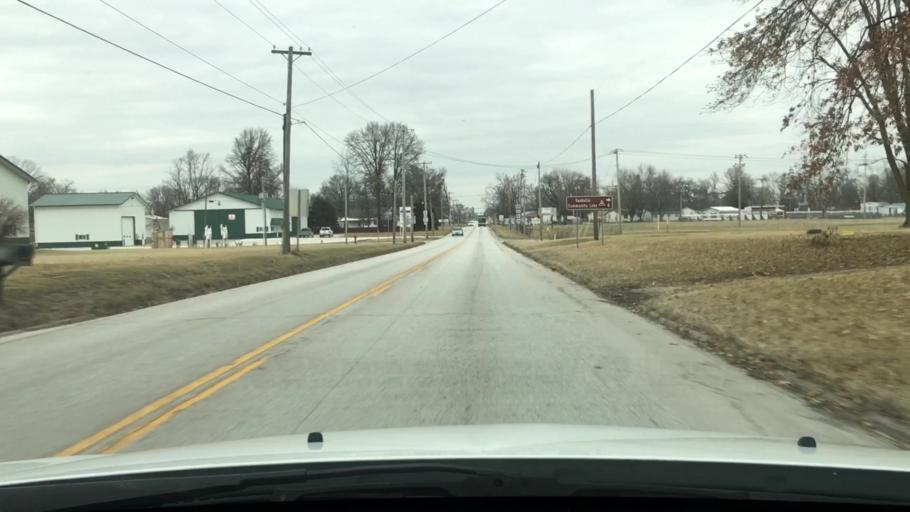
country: US
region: Missouri
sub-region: Audrain County
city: Vandalia
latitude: 39.2359
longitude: -91.6458
